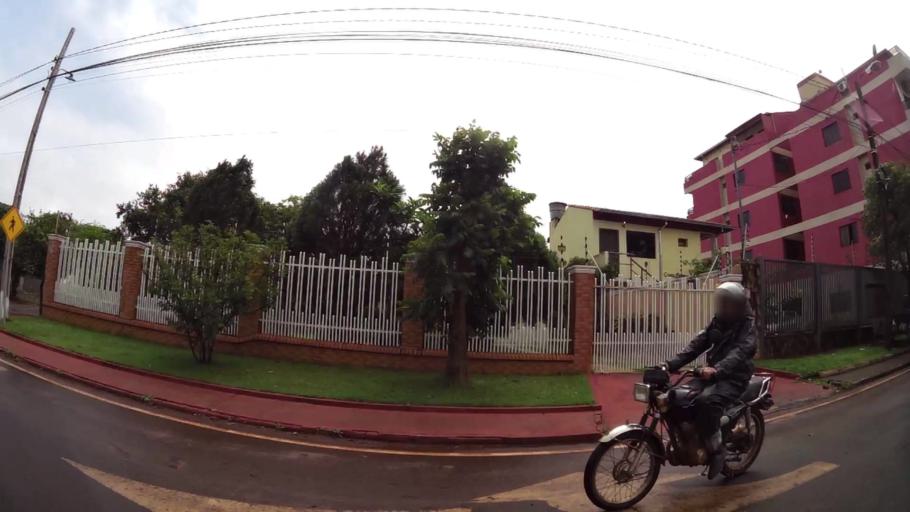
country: PY
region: Alto Parana
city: Ciudad del Este
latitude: -25.5107
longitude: -54.6437
